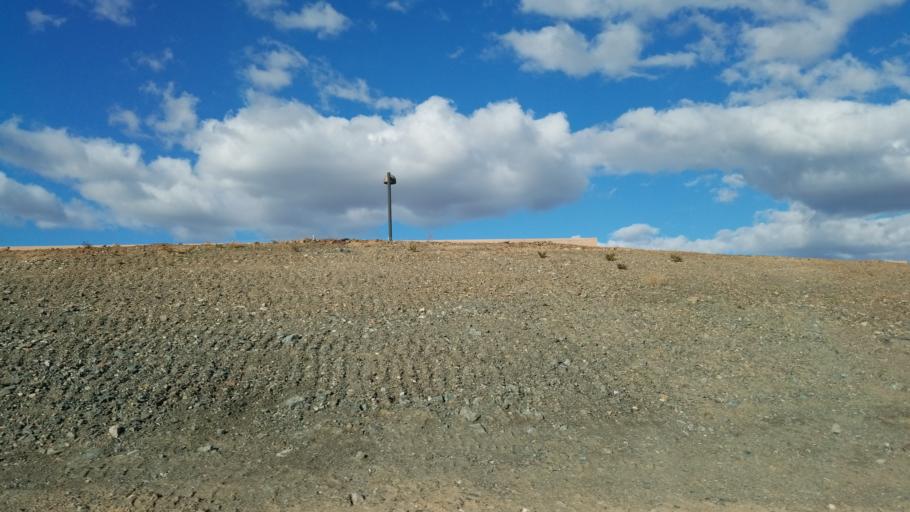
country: US
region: Arizona
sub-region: Maricopa County
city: Guadalupe
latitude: 33.2923
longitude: -112.0626
